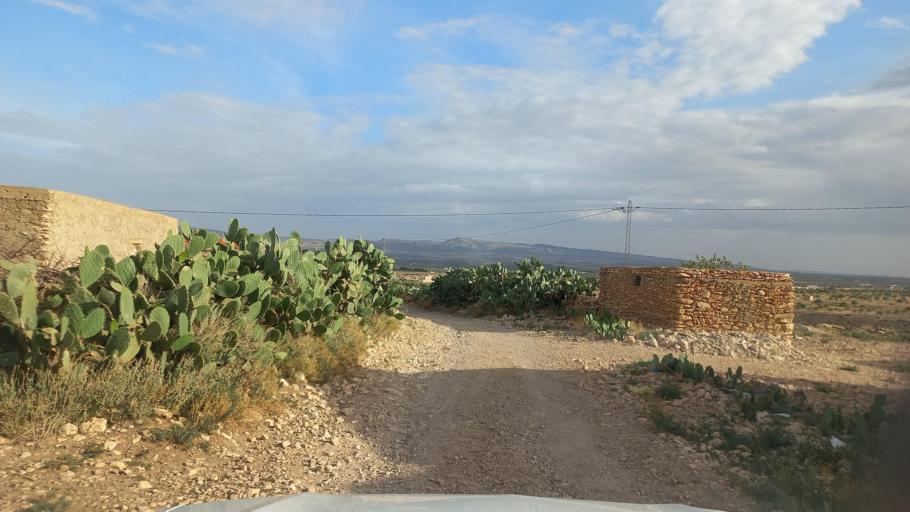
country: TN
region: Al Qasrayn
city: Sbiba
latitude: 35.4552
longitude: 9.0790
